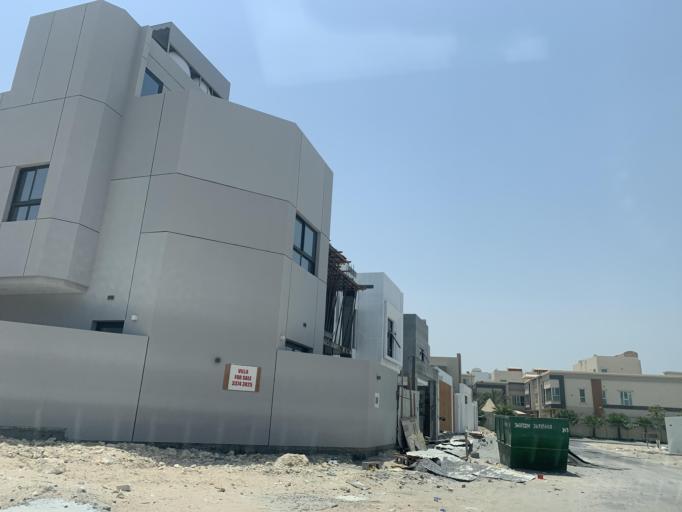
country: BH
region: Manama
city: Jidd Hafs
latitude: 26.2119
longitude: 50.4699
